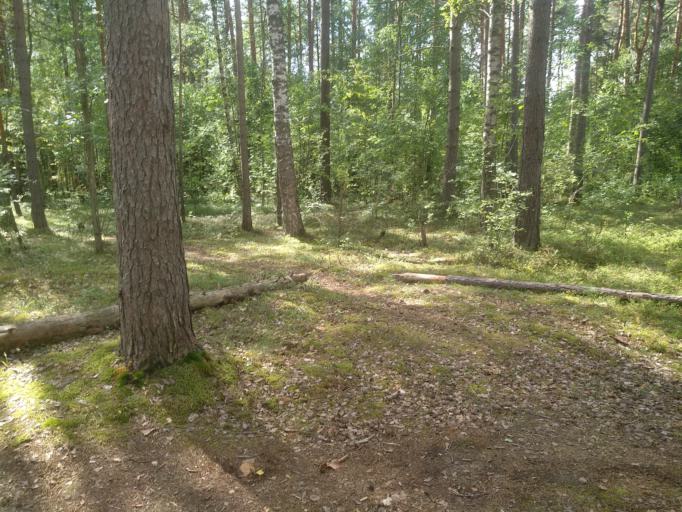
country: RU
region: Leningrad
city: Sapernoye
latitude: 60.6758
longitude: 29.9202
